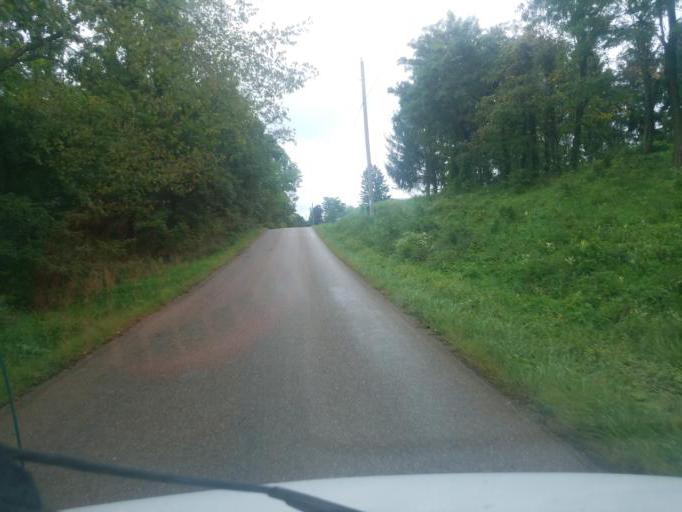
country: US
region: Ohio
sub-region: Wayne County
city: West Salem
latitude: 40.9453
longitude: -82.1000
